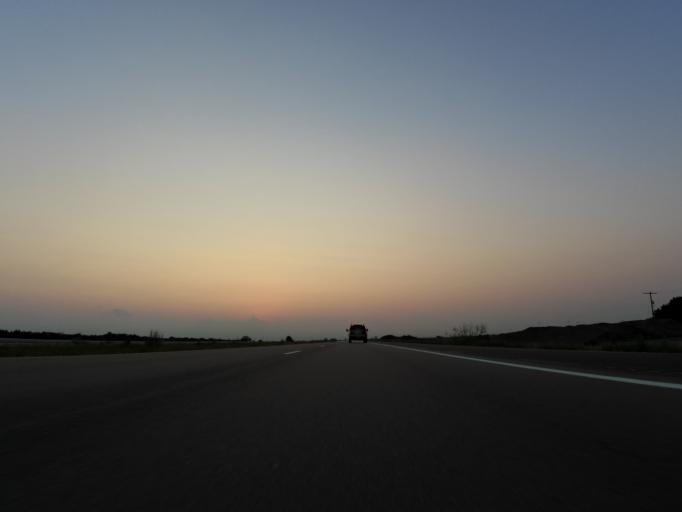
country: US
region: Kansas
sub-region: Reno County
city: South Hutchinson
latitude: 38.0142
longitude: -97.9936
